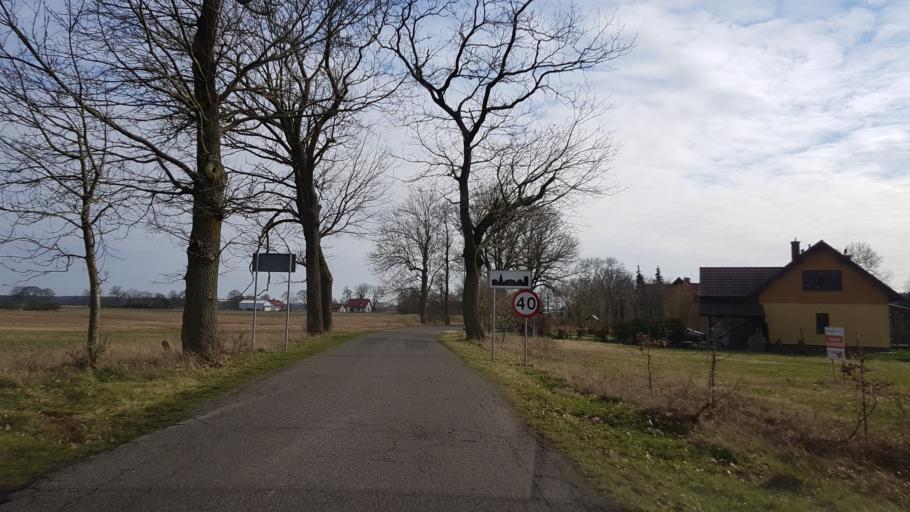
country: PL
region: West Pomeranian Voivodeship
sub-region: Powiat policki
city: Dobra
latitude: 53.5210
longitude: 14.3487
